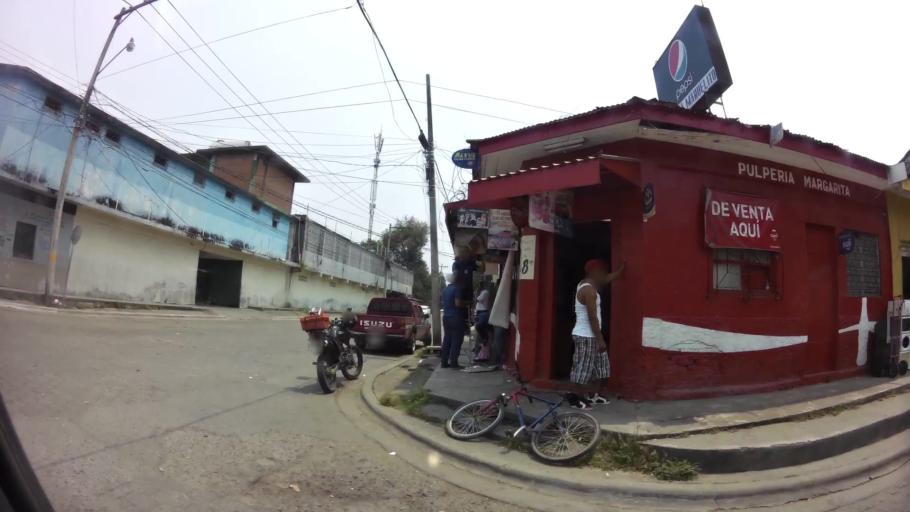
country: HN
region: Cortes
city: San Pedro Sula
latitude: 15.4991
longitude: -88.0138
